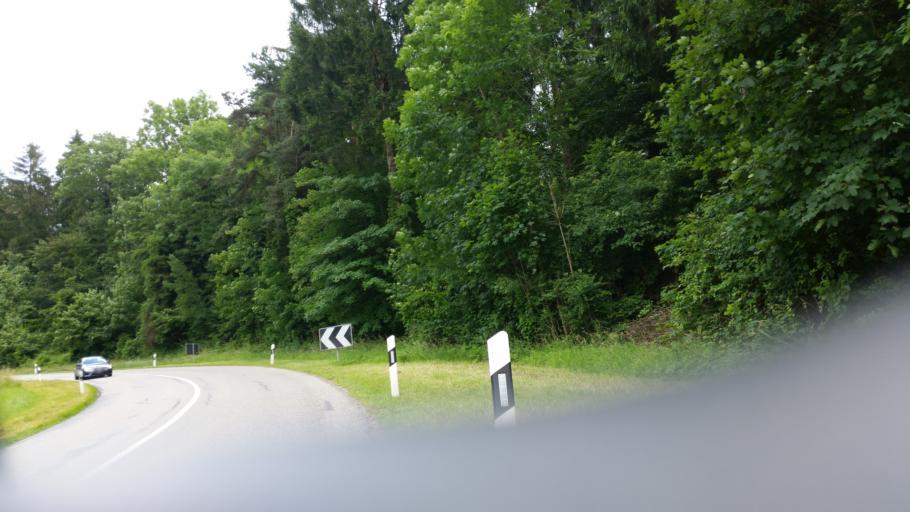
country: CH
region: Vaud
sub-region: Jura-Nord vaudois District
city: Yverdon-les-Bains
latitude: 46.7524
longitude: 6.6837
